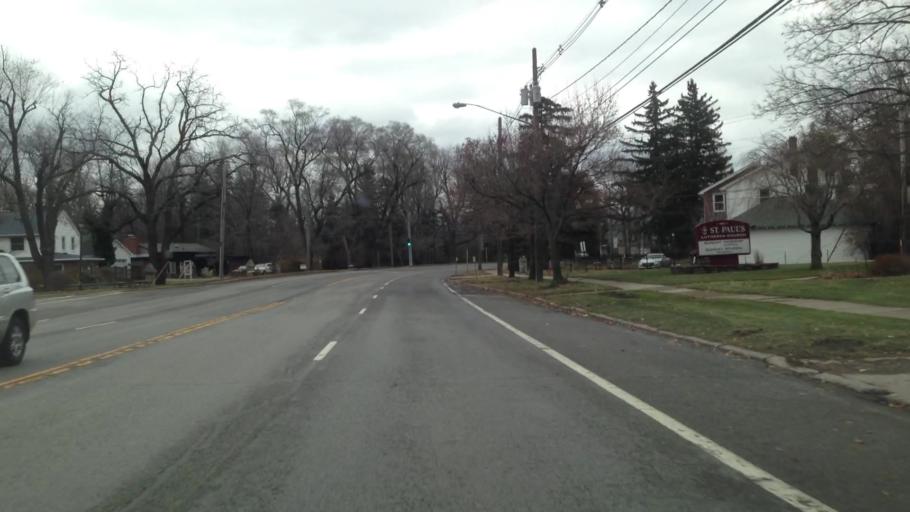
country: US
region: New York
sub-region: Erie County
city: Eggertsville
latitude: 42.9640
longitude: -78.8021
